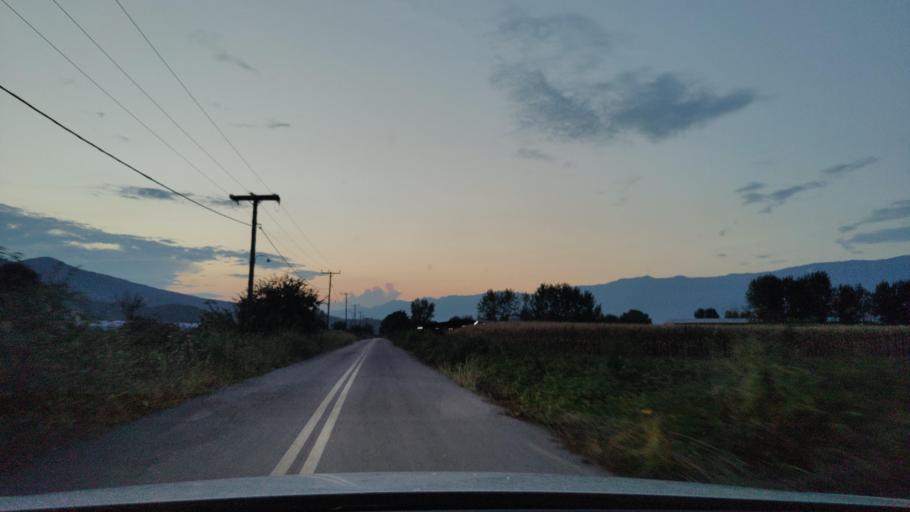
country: GR
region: Central Macedonia
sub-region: Nomos Serron
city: Chrysochorafa
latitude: 41.1794
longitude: 23.1107
